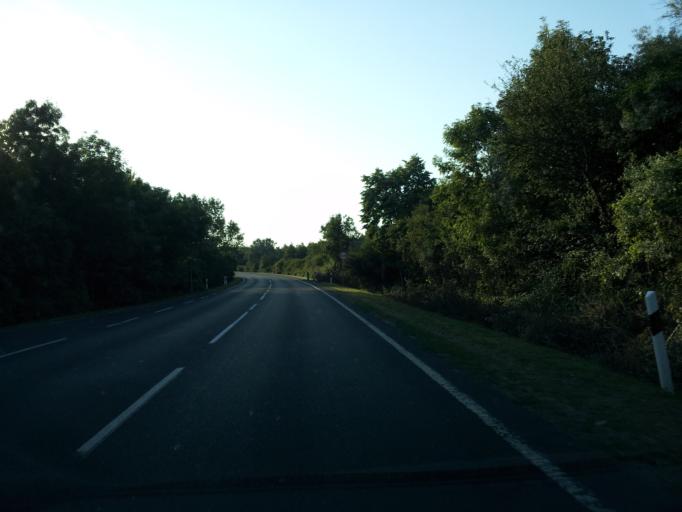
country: HU
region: Fejer
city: Szarliget
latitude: 47.4902
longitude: 18.5239
